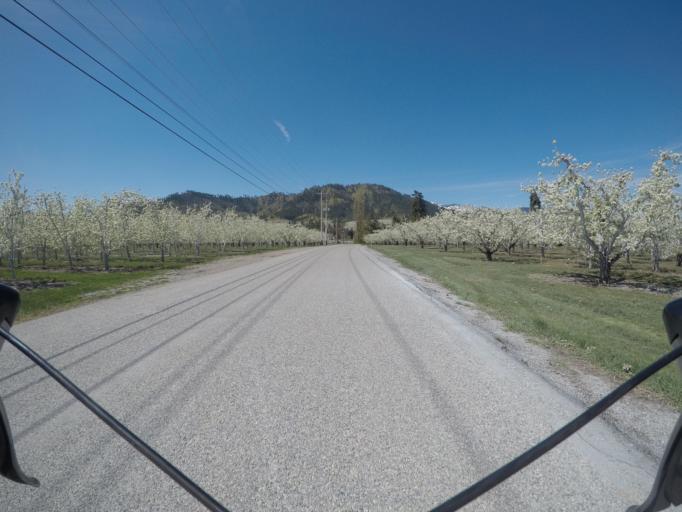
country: US
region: Washington
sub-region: Chelan County
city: Leavenworth
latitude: 47.5642
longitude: -120.5964
